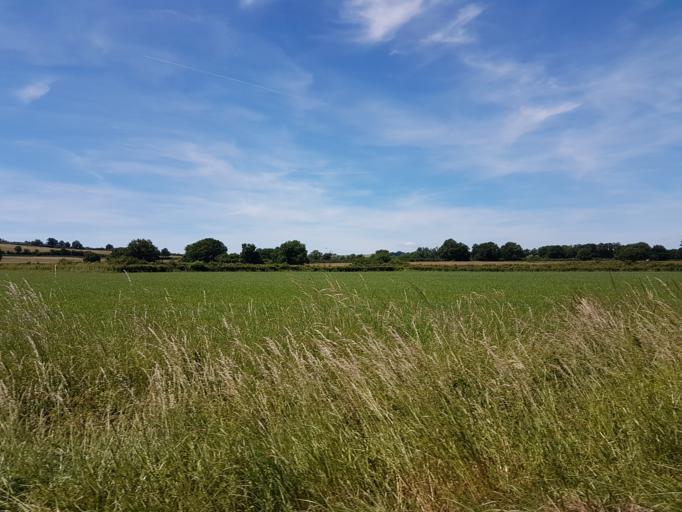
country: FR
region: Bourgogne
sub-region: Departement de Saone-et-Loire
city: Epinac
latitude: 46.9984
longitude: 4.4789
